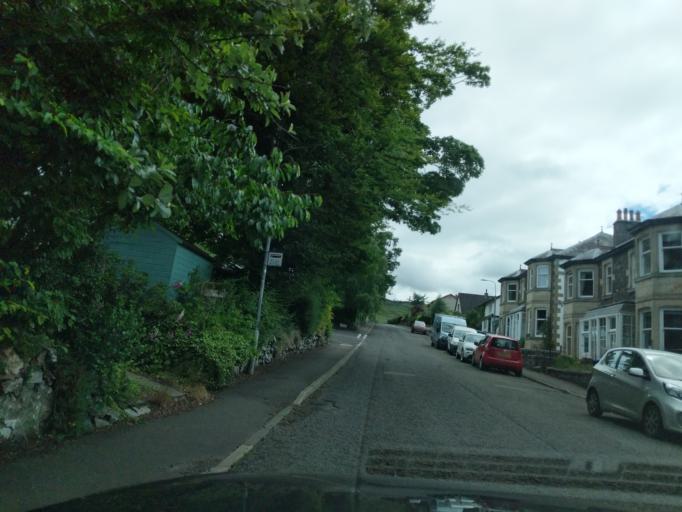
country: GB
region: Scotland
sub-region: The Scottish Borders
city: Peebles
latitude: 55.6478
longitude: -3.1989
